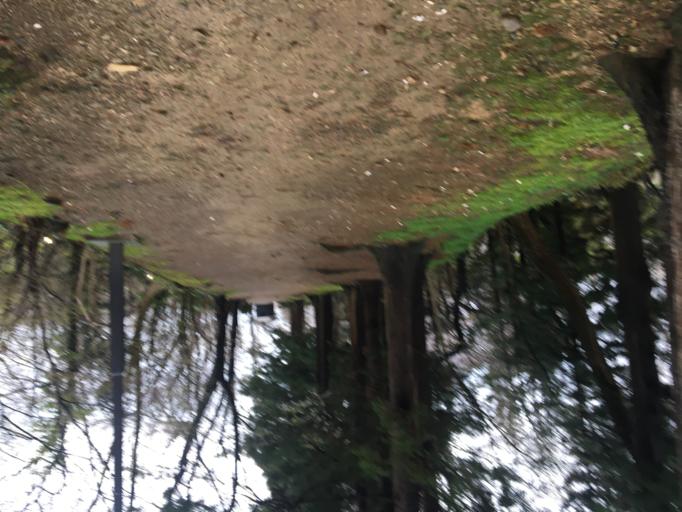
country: JP
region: Akita
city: Akita
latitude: 39.7232
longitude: 140.1242
